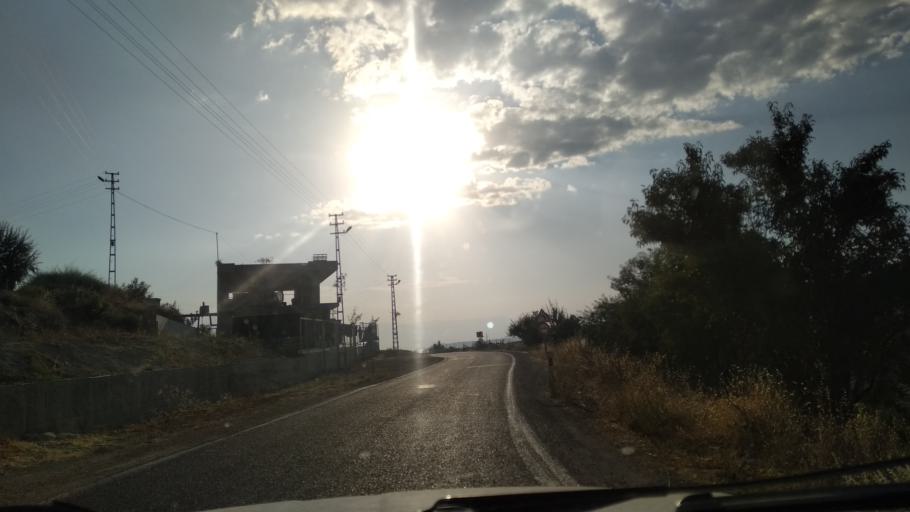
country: TR
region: Mersin
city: Sarikavak
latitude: 36.5771
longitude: 33.6432
